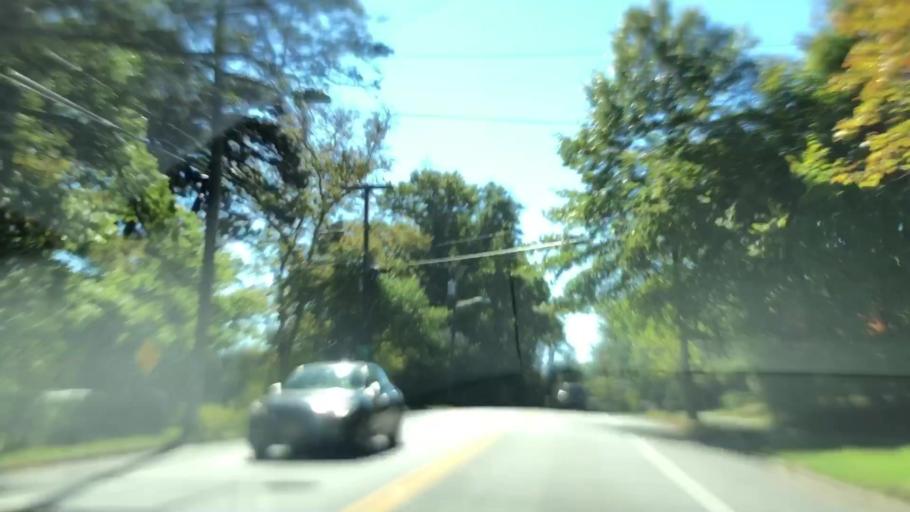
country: US
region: New Jersey
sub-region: Essex County
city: West Orange
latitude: 40.8022
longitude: -74.2253
